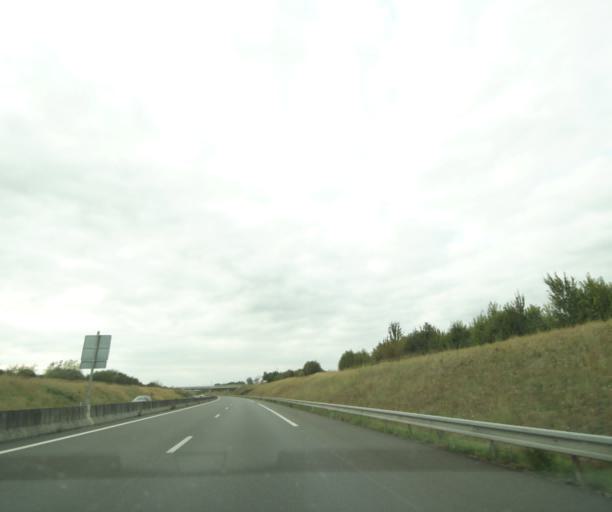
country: FR
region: Centre
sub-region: Departement d'Indre-et-Loire
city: Parcay-Meslay
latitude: 47.4781
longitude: 0.7526
